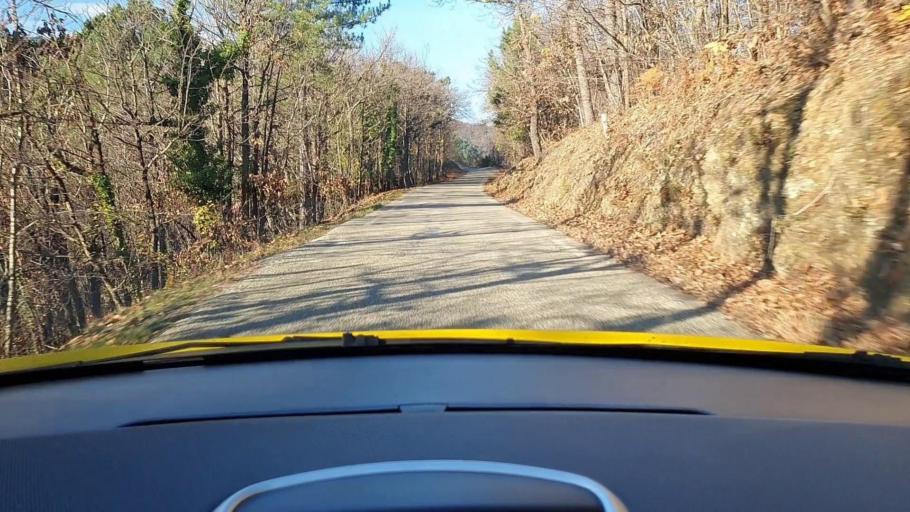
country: FR
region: Languedoc-Roussillon
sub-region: Departement du Gard
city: Branoux-les-Taillades
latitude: 44.2197
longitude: 3.9730
